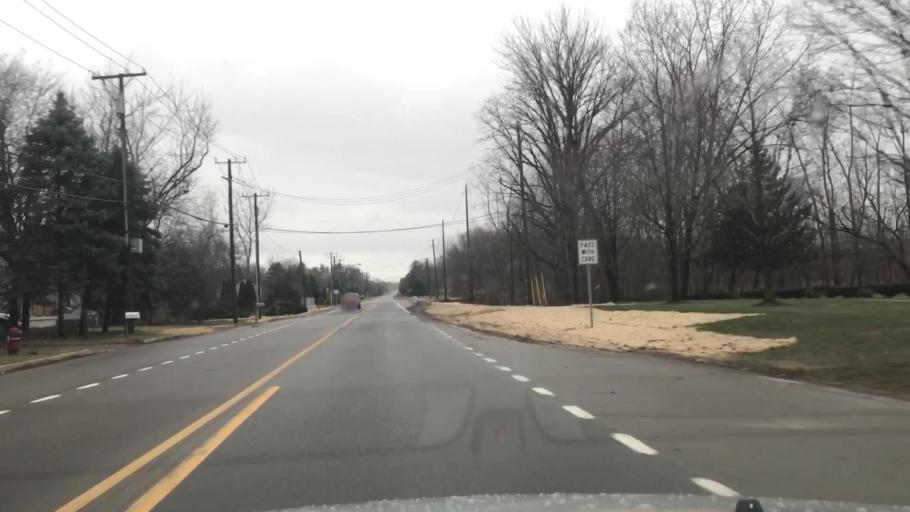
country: US
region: Michigan
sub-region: Oakland County
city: Troy
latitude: 42.6237
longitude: -83.1156
